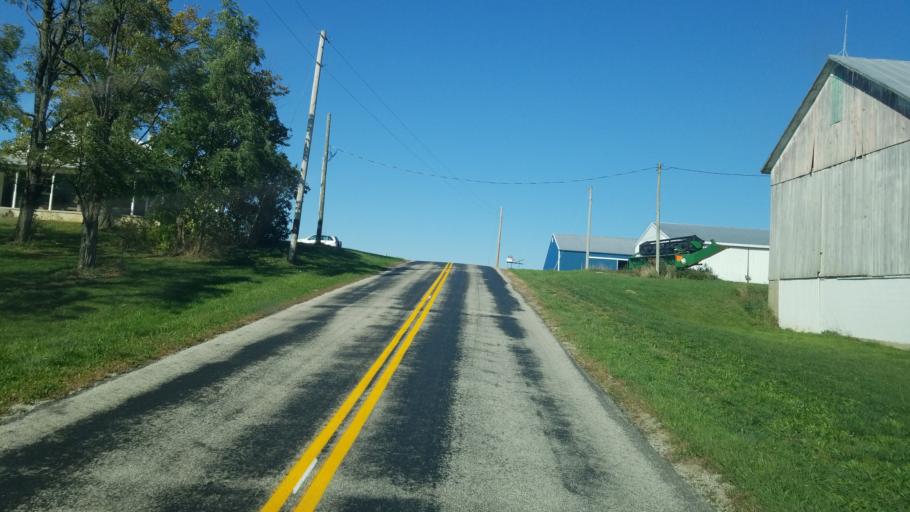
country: US
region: Ohio
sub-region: Huron County
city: New London
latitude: 41.0111
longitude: -82.3739
